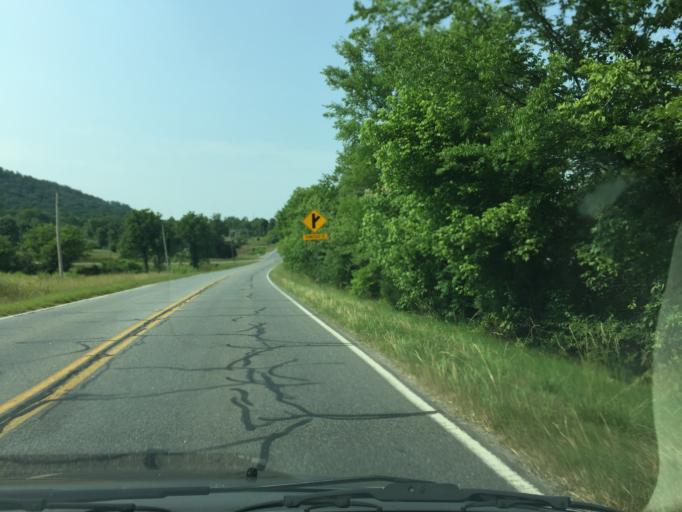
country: US
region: Georgia
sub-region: Catoosa County
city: Ringgold
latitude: 34.9286
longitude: -85.1038
